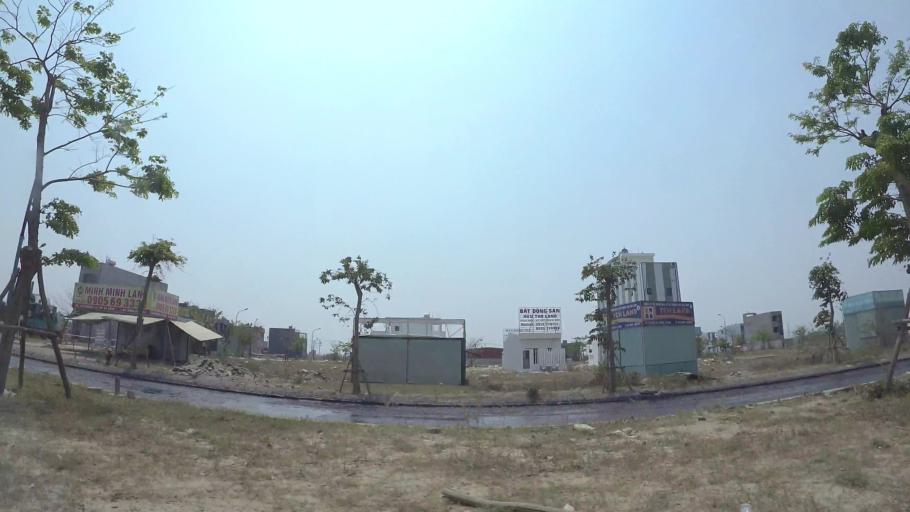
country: VN
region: Da Nang
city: Ngu Hanh Son
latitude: 16.0127
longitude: 108.2384
